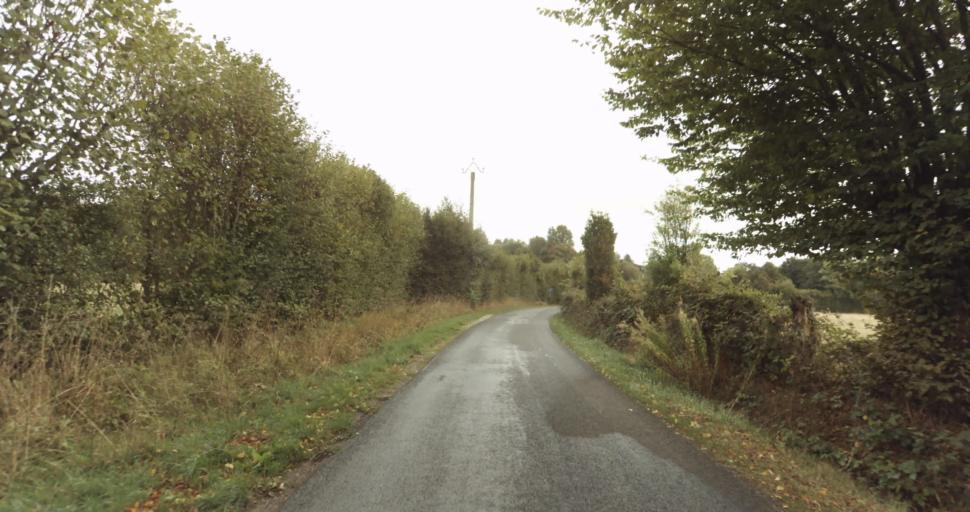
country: FR
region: Lower Normandy
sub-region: Departement de l'Orne
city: Sainte-Gauburge-Sainte-Colombe
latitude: 48.7451
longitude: 0.4726
